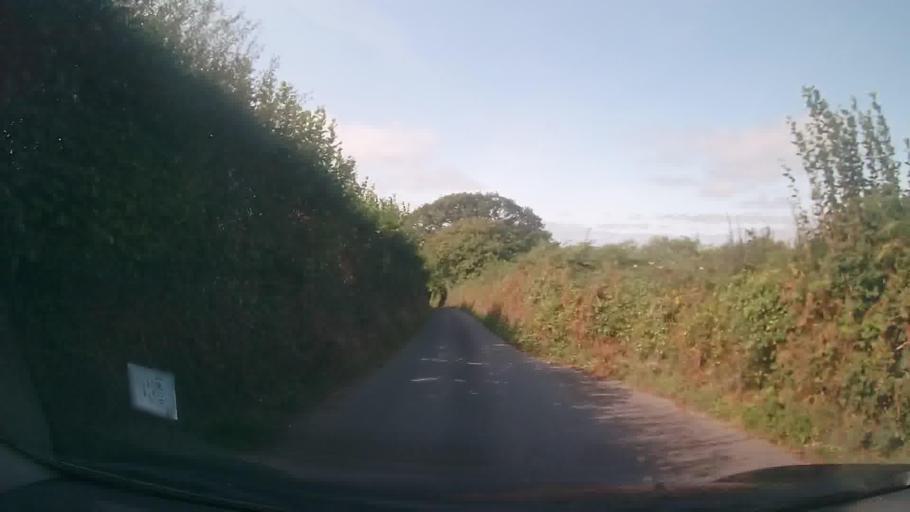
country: GB
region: Wales
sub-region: Pembrokeshire
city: Saundersfoot
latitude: 51.7415
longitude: -4.6641
